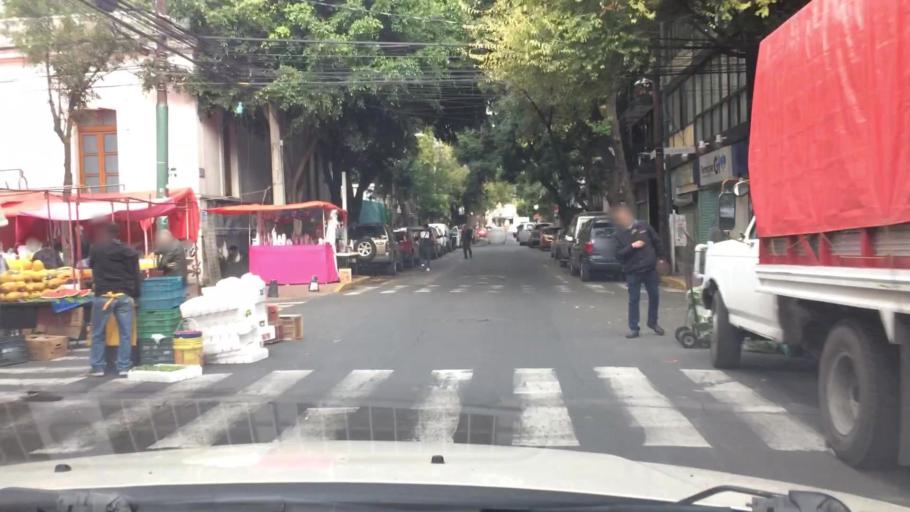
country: MX
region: Mexico City
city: Benito Juarez
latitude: 19.4029
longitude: -99.1800
